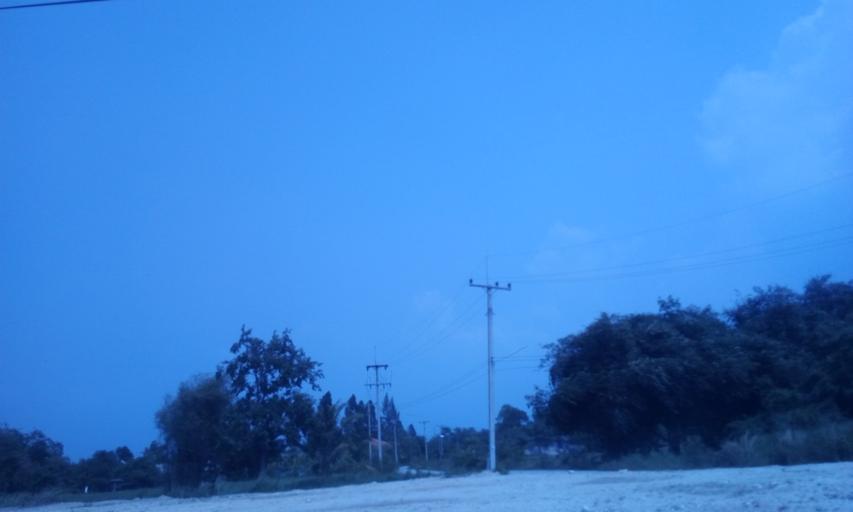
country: TH
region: Chon Buri
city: Phanat Nikhom
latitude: 13.3775
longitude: 101.1945
